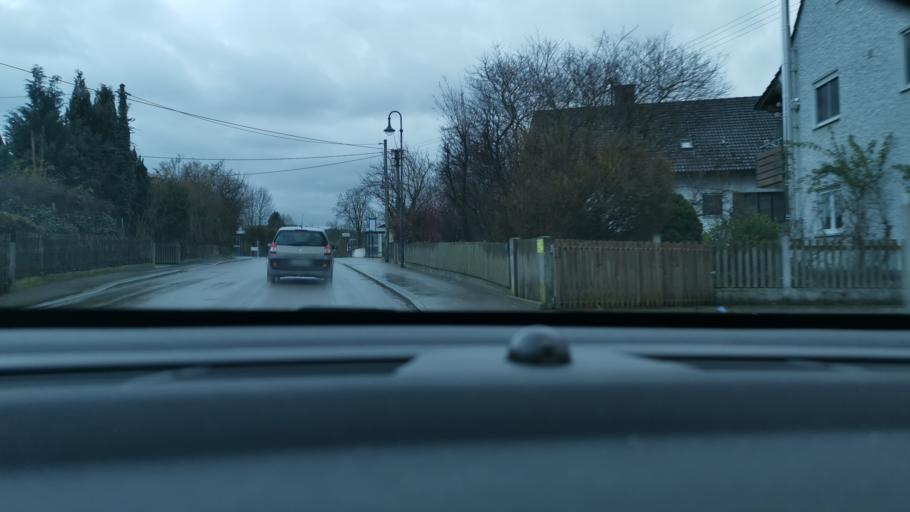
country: DE
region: Bavaria
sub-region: Swabia
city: Affing
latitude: 48.4552
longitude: 10.9810
